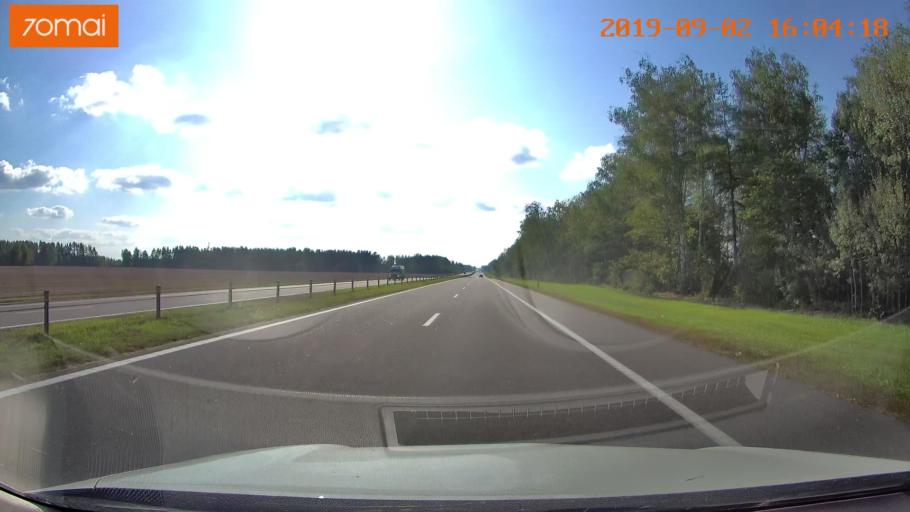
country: BY
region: Minsk
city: Byerazino
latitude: 53.7992
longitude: 28.8467
